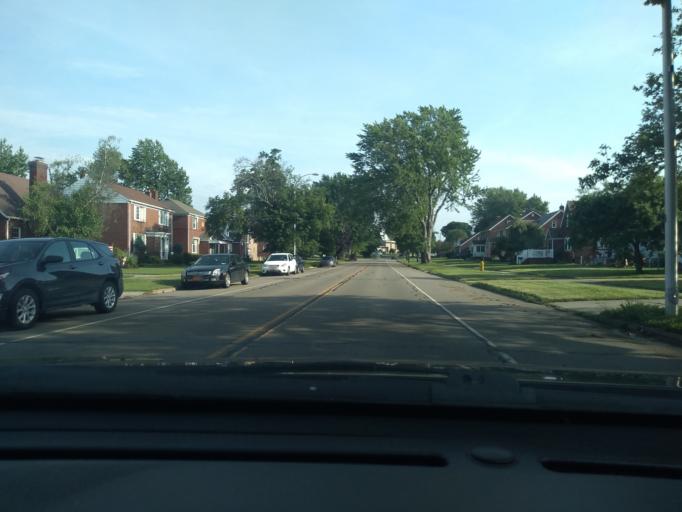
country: US
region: New York
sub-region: Erie County
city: Lackawanna
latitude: 42.8308
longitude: -78.8086
